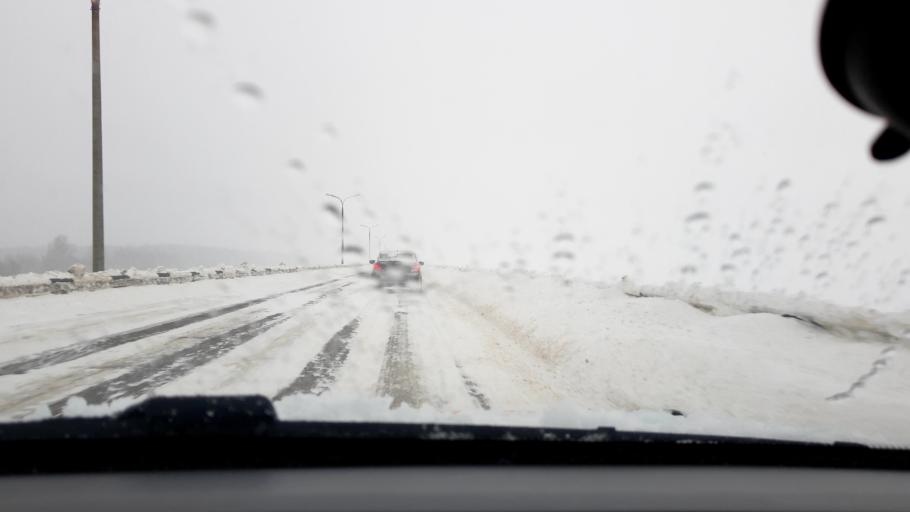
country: RU
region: Nizjnij Novgorod
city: Pervomayskiy
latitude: 56.6430
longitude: 43.3170
